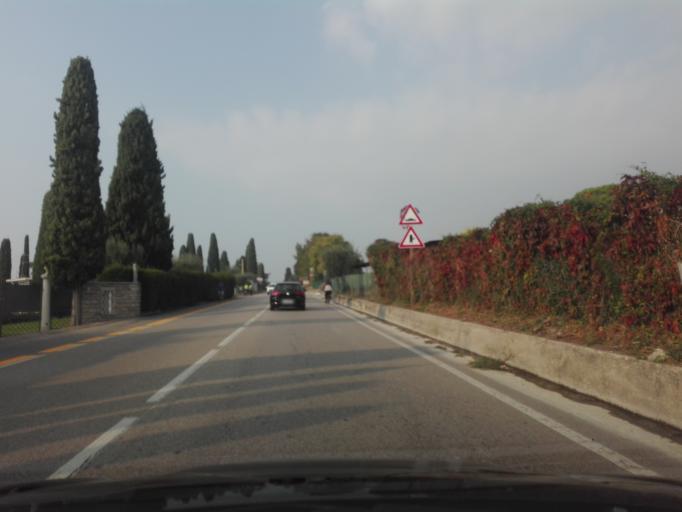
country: IT
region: Veneto
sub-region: Provincia di Verona
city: Lazise
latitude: 45.5159
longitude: 10.7311
